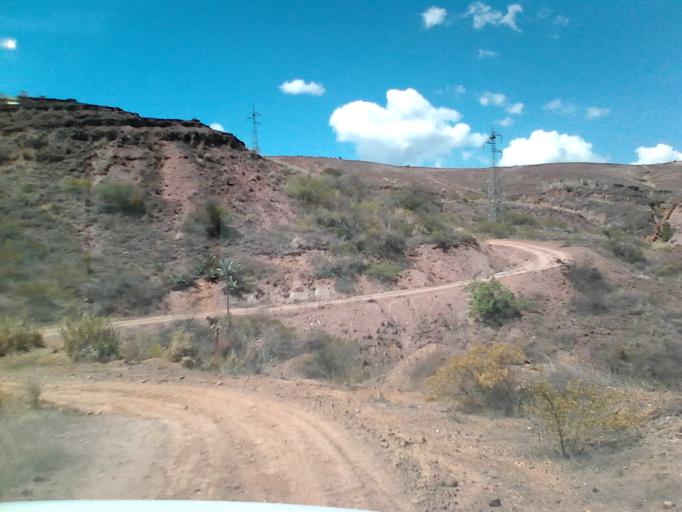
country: CO
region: Boyaca
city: Sachica
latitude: 5.6051
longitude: -73.5729
